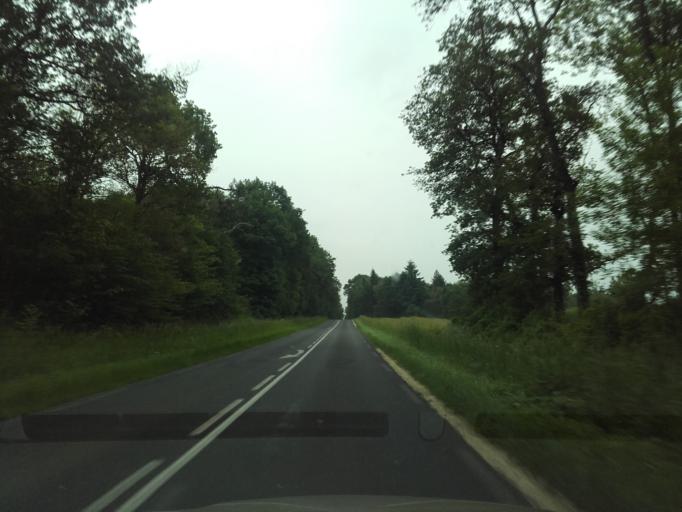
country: FR
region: Centre
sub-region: Departement d'Indre-et-Loire
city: Beaumont-la-Ronce
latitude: 47.5917
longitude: 0.6648
